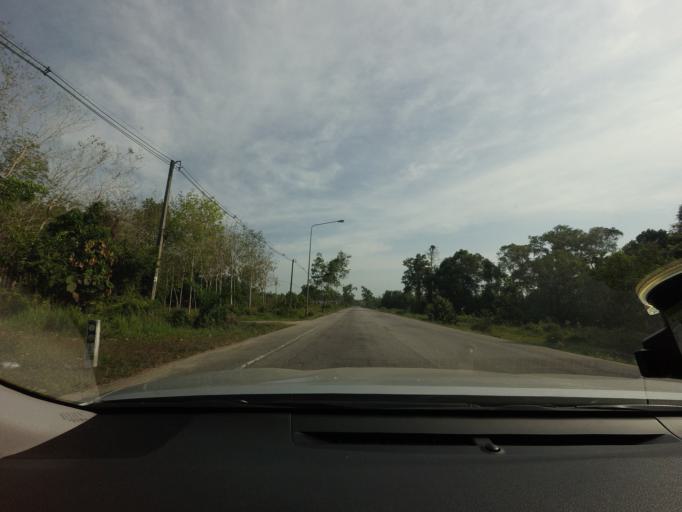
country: TH
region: Narathiwat
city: Narathiwat
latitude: 6.3651
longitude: 101.7905
